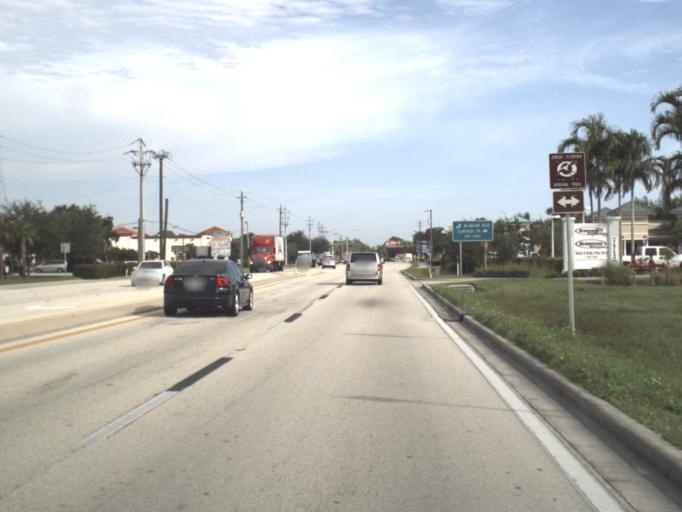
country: US
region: Florida
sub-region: Lee County
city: Harlem Heights
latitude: 26.5126
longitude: -81.9437
